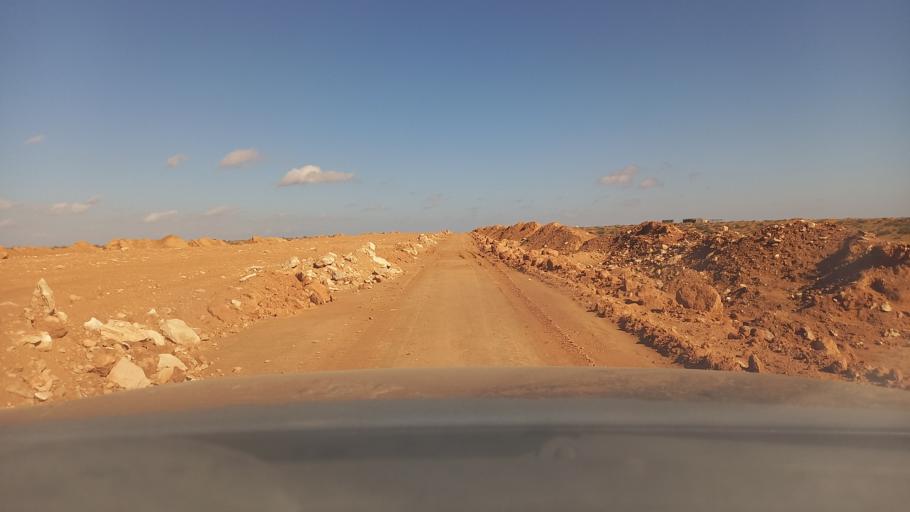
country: TN
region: Madanin
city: Medenine
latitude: 33.2427
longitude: 10.5578
